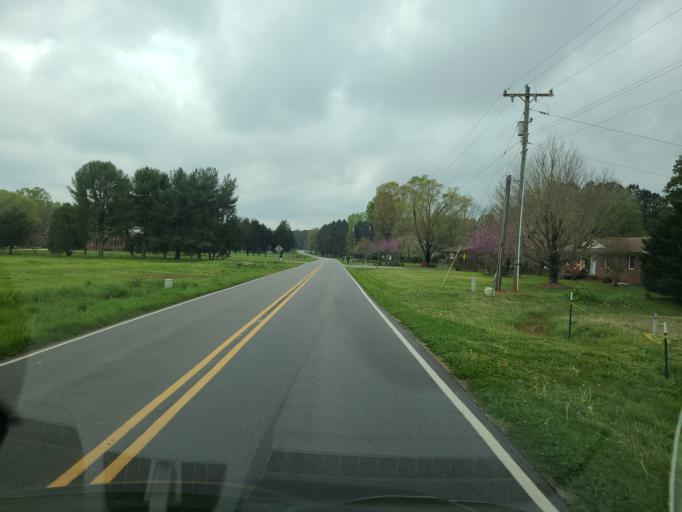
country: US
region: North Carolina
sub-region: Lincoln County
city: Lincolnton
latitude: 35.4620
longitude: -81.2982
